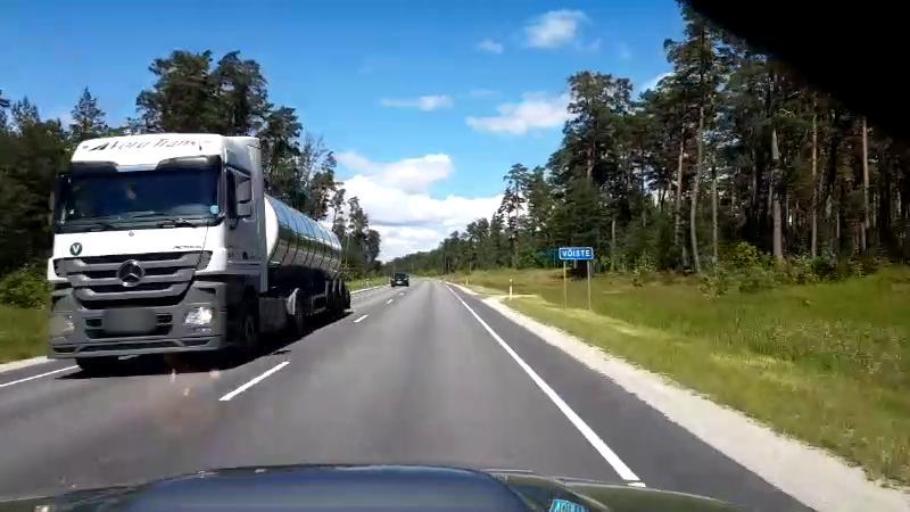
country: EE
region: Paernumaa
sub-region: Paernu linn
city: Parnu
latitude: 58.1900
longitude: 24.4909
